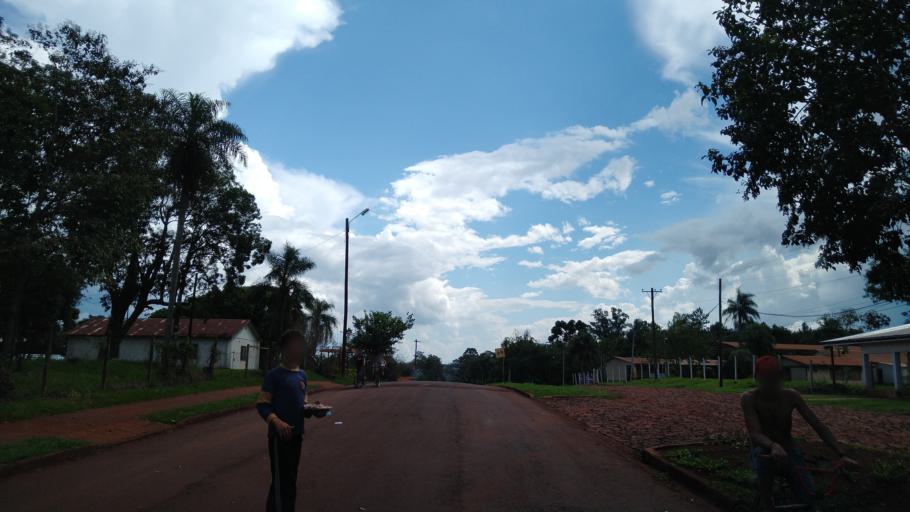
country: AR
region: Misiones
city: Puerto Libertad
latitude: -25.9668
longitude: -54.5923
